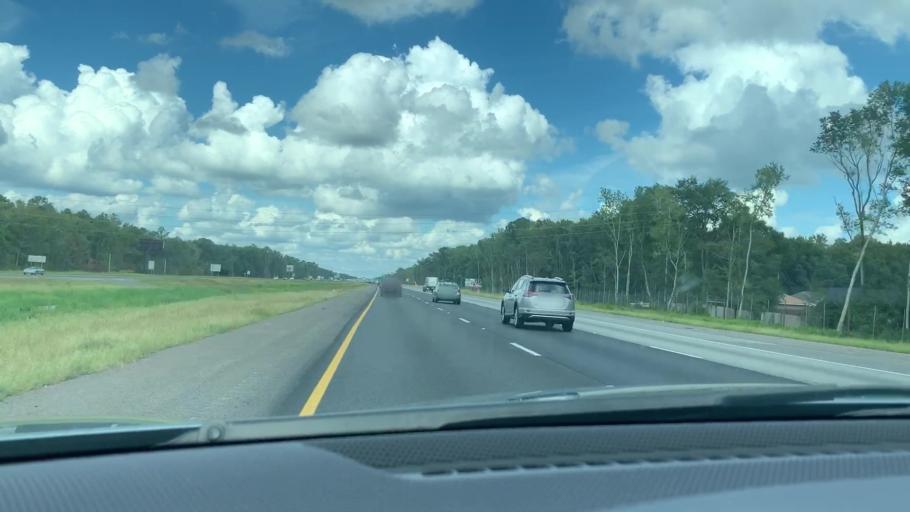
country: US
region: Georgia
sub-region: Camden County
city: Kingsland
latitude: 30.7980
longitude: -81.6602
